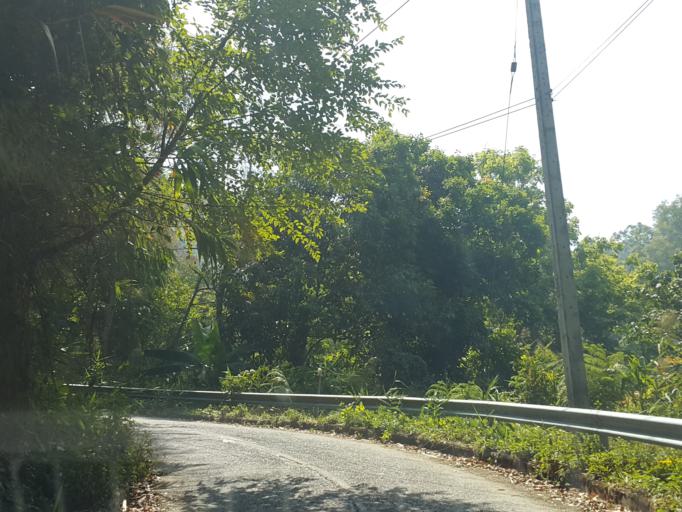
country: TH
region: Chiang Mai
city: Mae On
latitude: 18.8593
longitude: 99.3551
